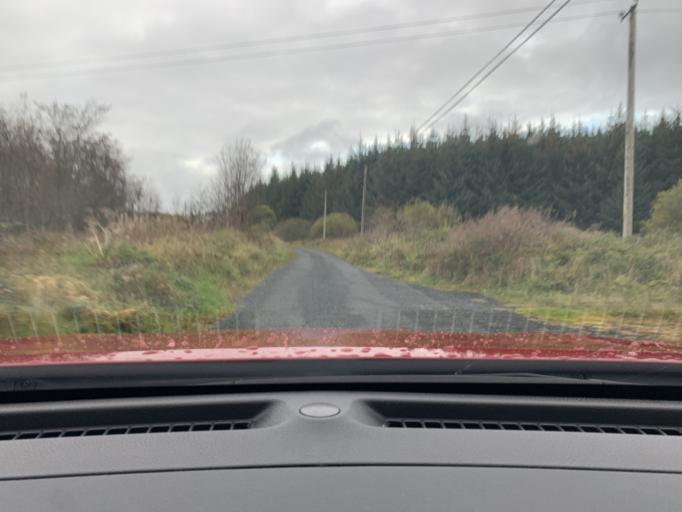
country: IE
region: Connaught
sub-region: Roscommon
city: Ballaghaderreen
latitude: 53.9731
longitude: -8.6003
